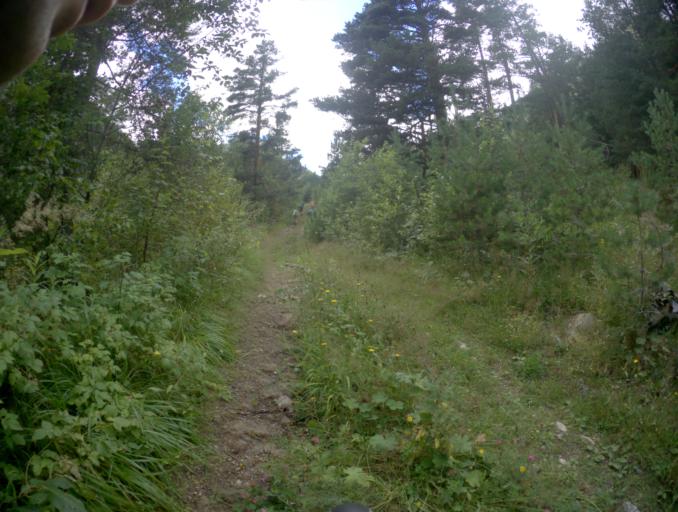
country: RU
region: Karachayevo-Cherkesiya
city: Uchkulan
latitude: 43.3533
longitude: 42.1625
